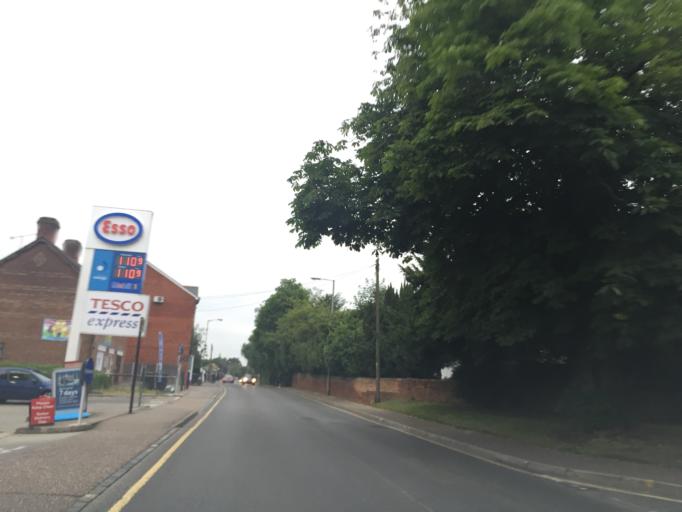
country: GB
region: England
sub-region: Essex
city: Chipping Ongar
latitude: 51.7068
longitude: 0.2450
